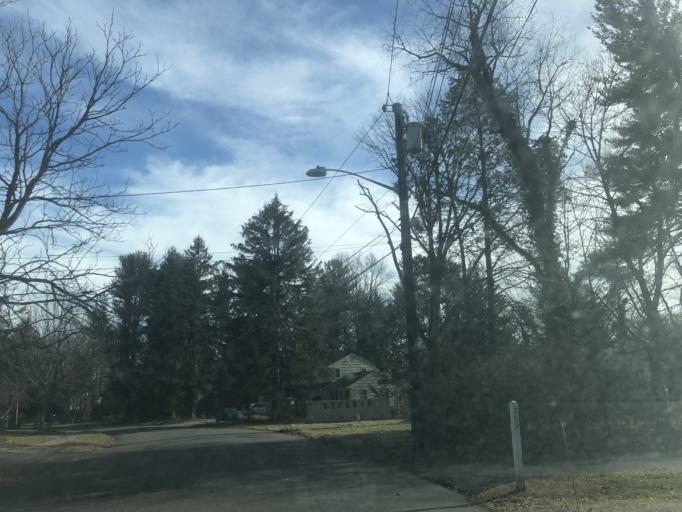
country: US
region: New Jersey
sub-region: Mercer County
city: Princeton
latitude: 40.3512
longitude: -74.6329
